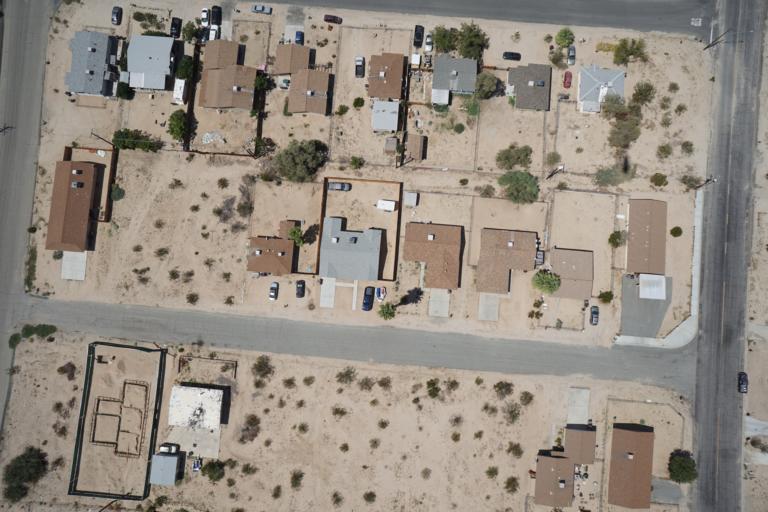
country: US
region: California
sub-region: San Bernardino County
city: Twentynine Palms
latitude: 34.1386
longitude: -116.0478
